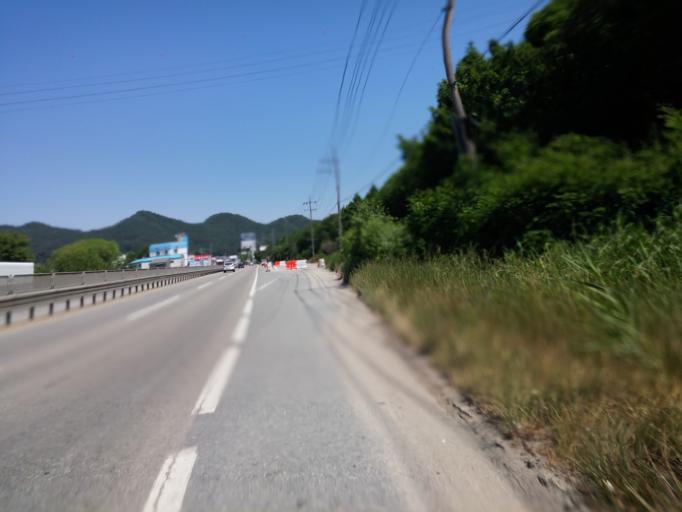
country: KR
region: Daejeon
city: Sintansin
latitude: 36.5260
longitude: 127.4316
